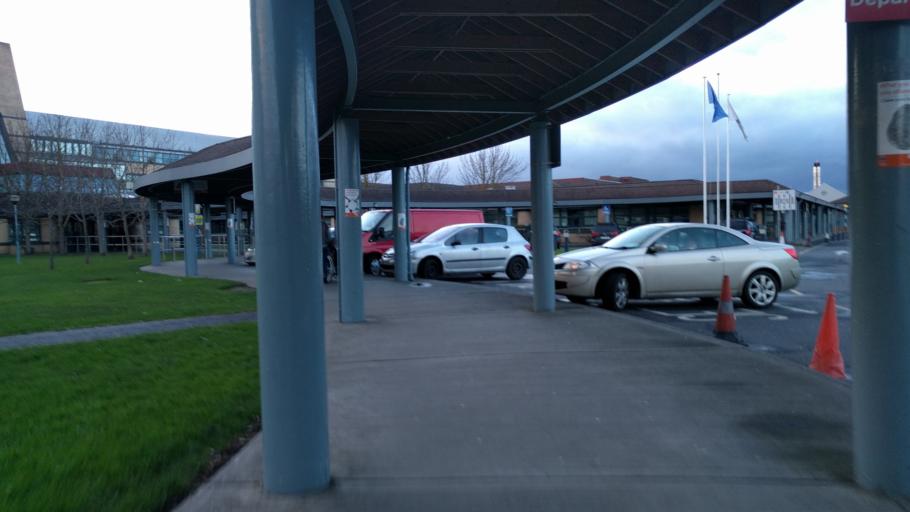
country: IE
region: Leinster
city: Tallaght
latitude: 53.2909
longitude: -6.3769
